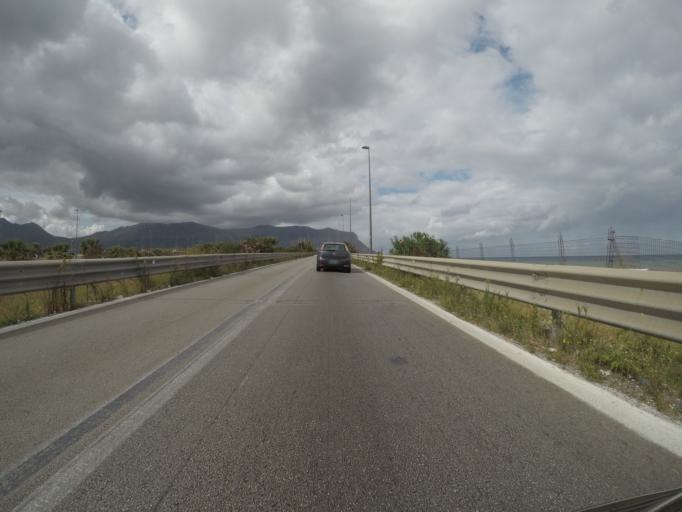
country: IT
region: Sicily
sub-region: Palermo
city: Capaci
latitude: 38.1755
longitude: 13.2168
